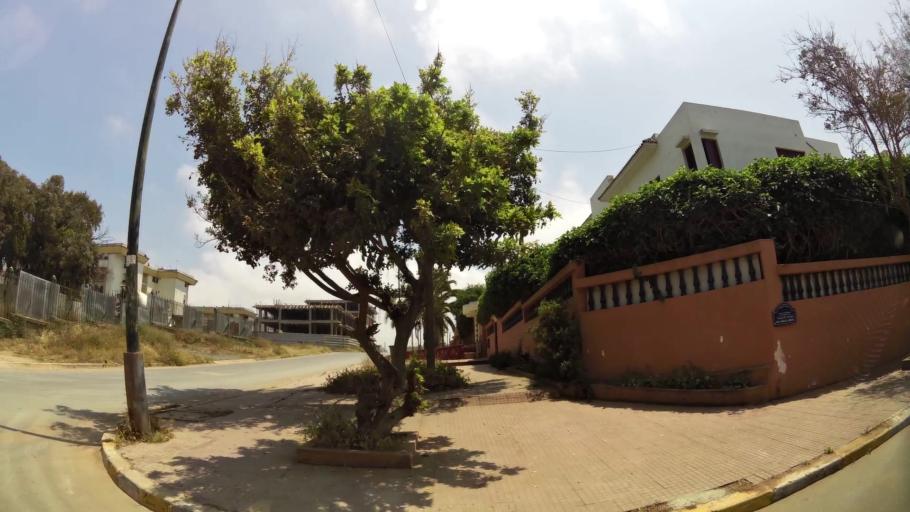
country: MA
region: Rabat-Sale-Zemmour-Zaer
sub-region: Skhirate-Temara
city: Temara
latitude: 33.9716
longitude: -6.8996
